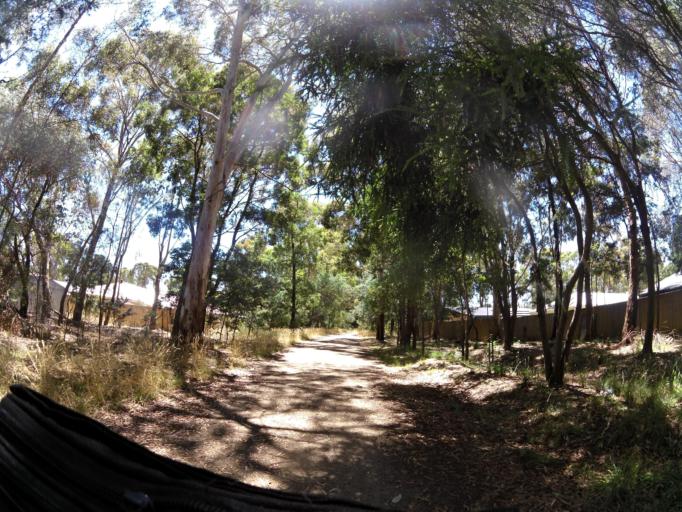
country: AU
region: Victoria
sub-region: Ballarat North
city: Delacombe
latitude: -37.6409
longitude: 143.6845
